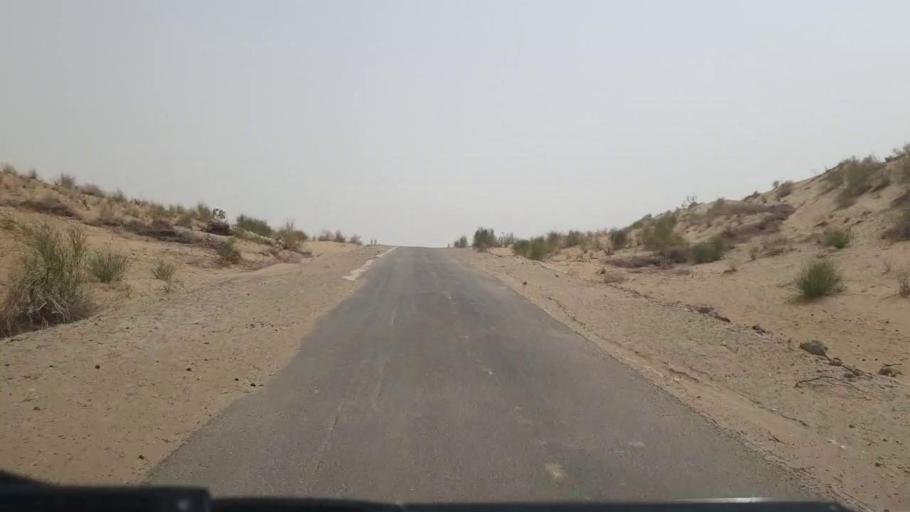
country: PK
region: Sindh
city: Islamkot
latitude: 25.2742
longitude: 70.6538
